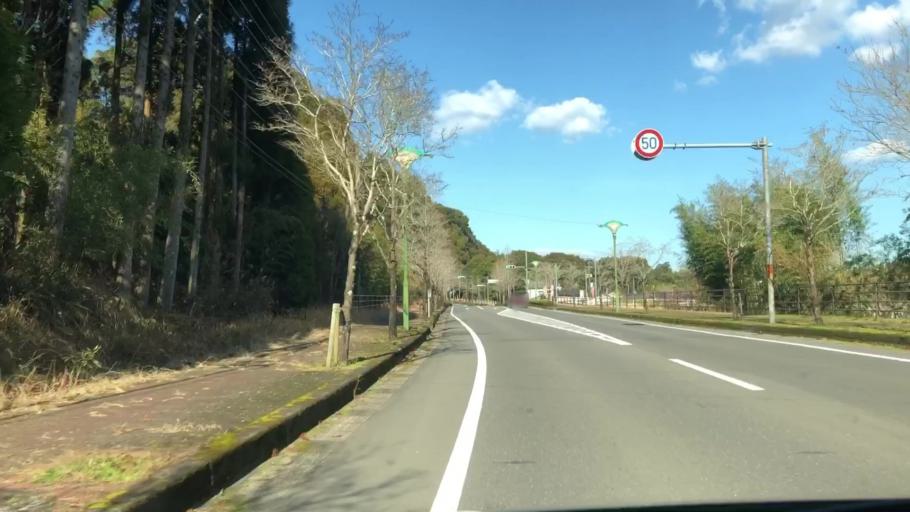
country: JP
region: Kagoshima
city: Satsumasendai
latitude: 31.8259
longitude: 130.4346
